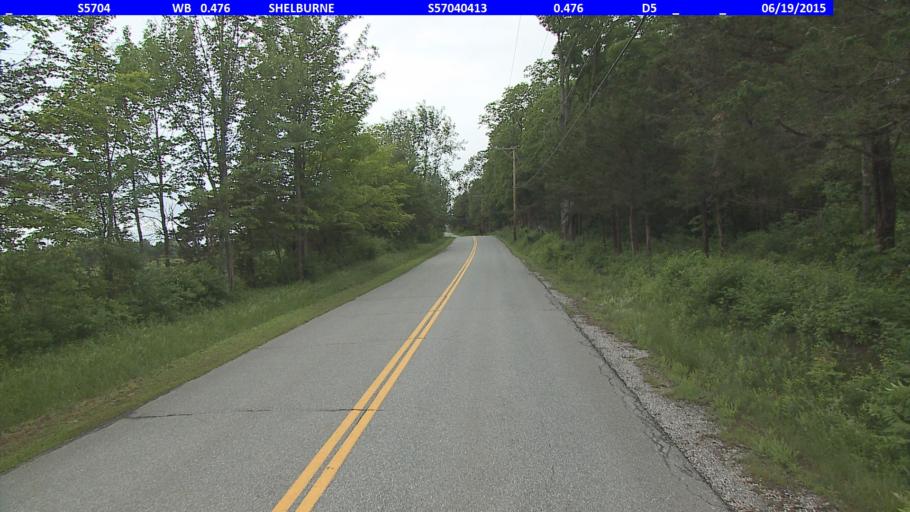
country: US
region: Vermont
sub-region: Chittenden County
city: Burlington
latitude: 44.3980
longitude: -73.2381
